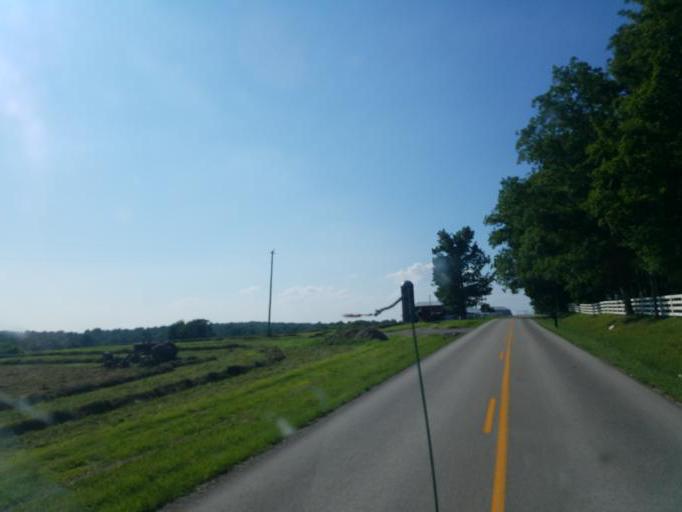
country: US
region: Kentucky
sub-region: Hart County
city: Munfordville
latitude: 37.3179
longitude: -86.0609
